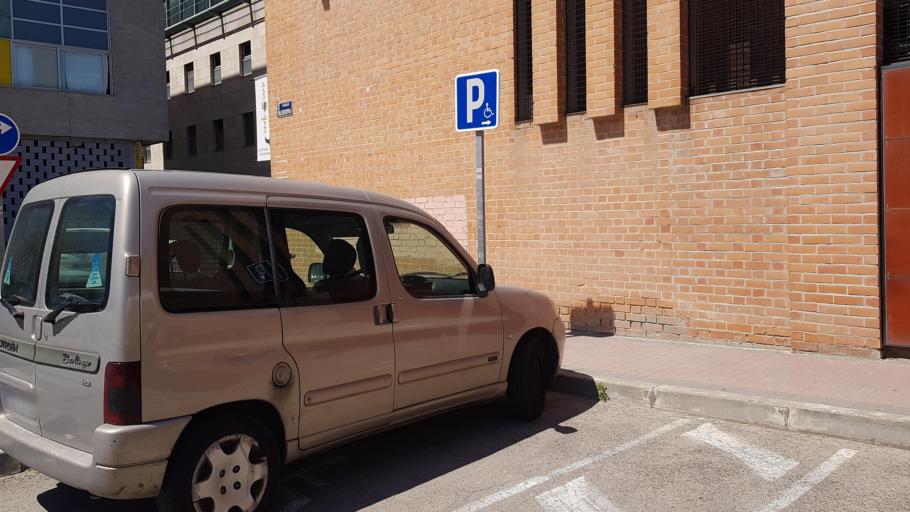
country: ES
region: Madrid
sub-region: Provincia de Madrid
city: Pinar de Chamartin
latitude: 40.4884
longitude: -3.6877
